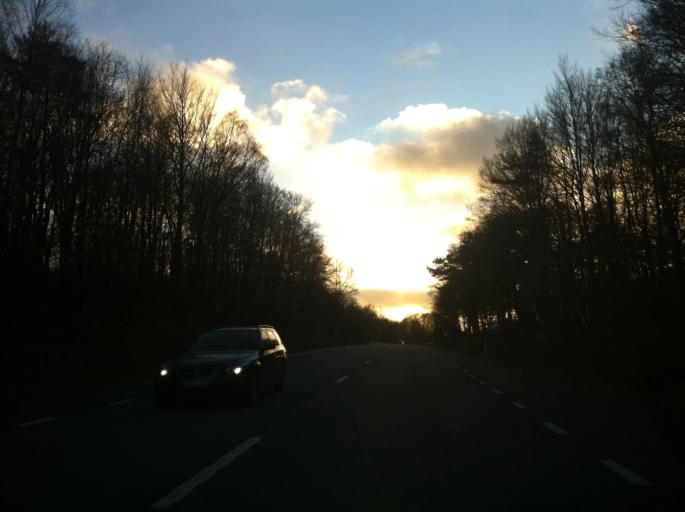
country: SE
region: Skane
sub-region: Hassleholms Kommun
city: Sosdala
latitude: 56.0259
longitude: 13.6757
